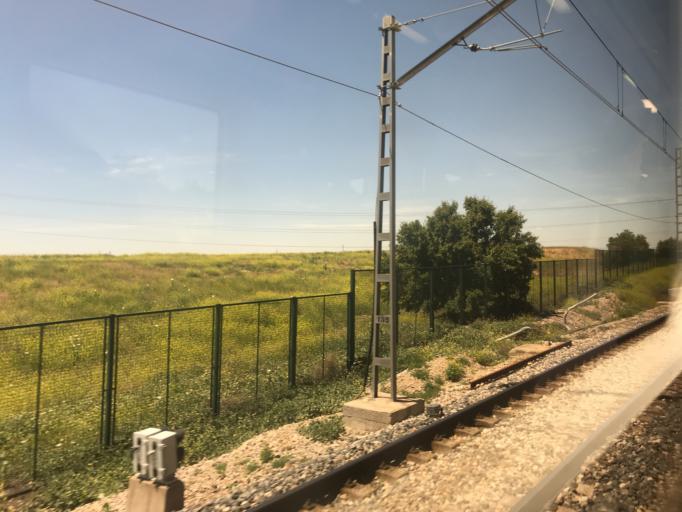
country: ES
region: Madrid
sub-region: Provincia de Madrid
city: Pinto
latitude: 40.2604
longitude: -3.7044
